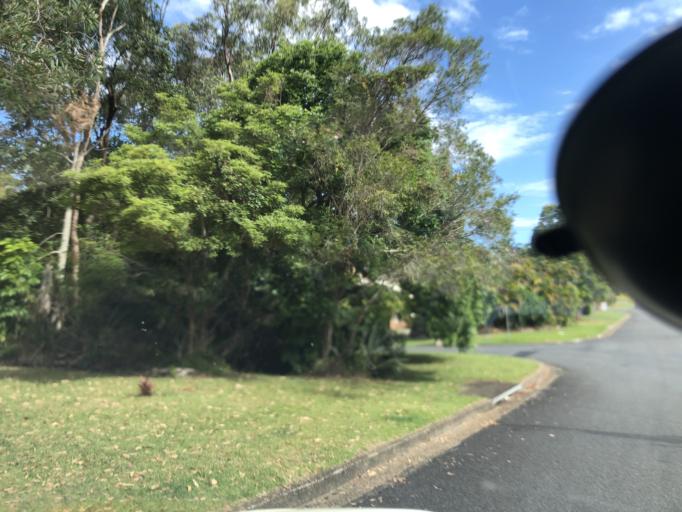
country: AU
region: New South Wales
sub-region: Coffs Harbour
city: Moonee Beach
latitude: -30.2355
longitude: 153.1488
